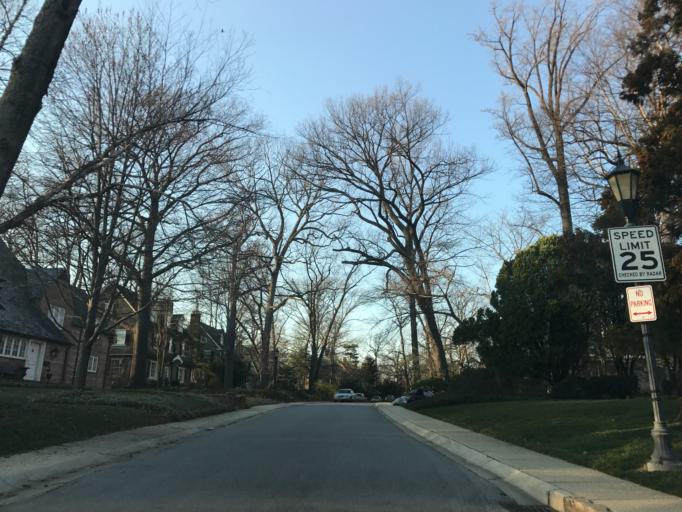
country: US
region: Maryland
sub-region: City of Baltimore
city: Baltimore
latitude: 39.3428
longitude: -76.6135
